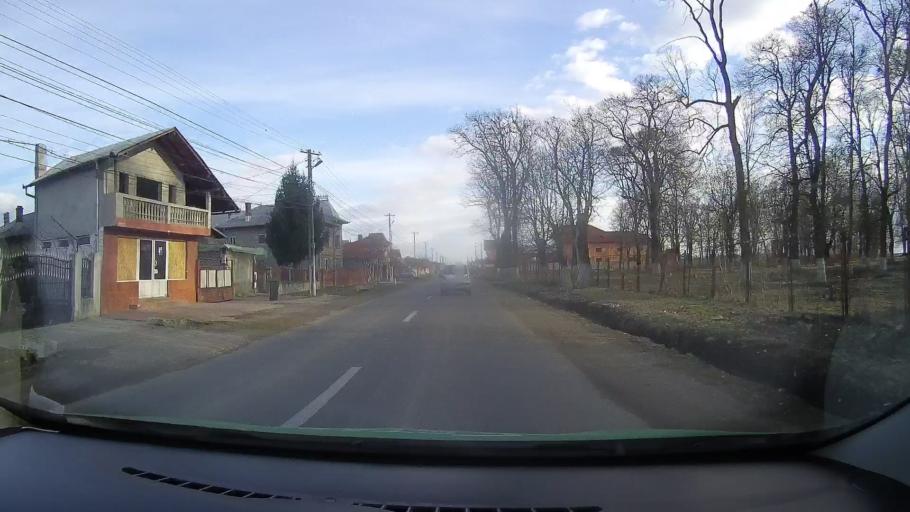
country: RO
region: Dambovita
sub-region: Comuna Vacaresti
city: Vacaresti
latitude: 44.8583
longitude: 25.4829
